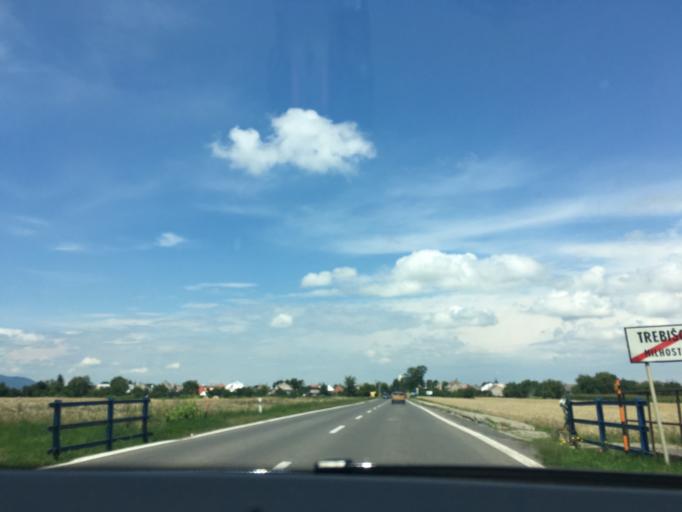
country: SK
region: Kosicky
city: Trebisov
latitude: 48.6700
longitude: 21.7123
